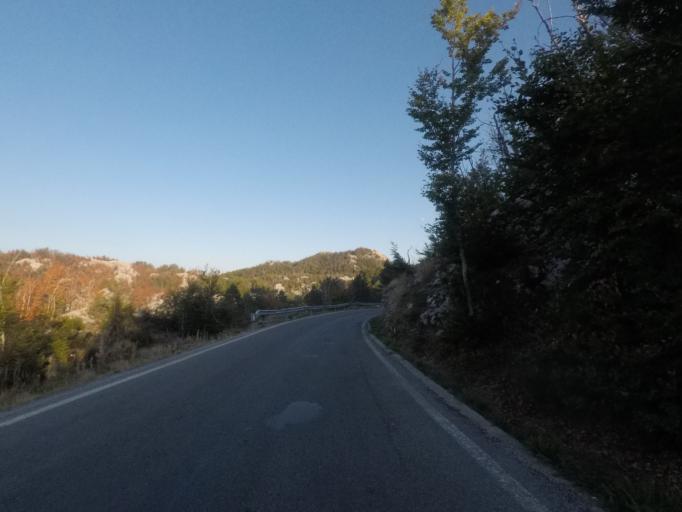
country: ME
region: Cetinje
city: Cetinje
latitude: 42.3806
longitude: 18.8461
